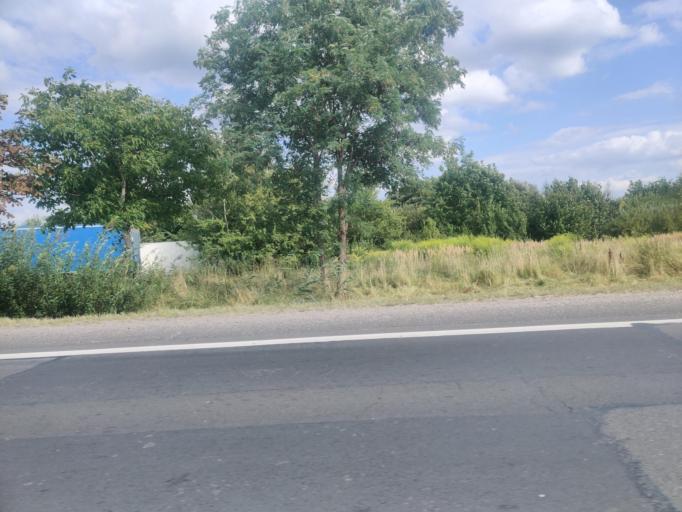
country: PL
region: Greater Poland Voivodeship
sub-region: Konin
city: Konin
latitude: 52.1938
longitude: 18.2673
